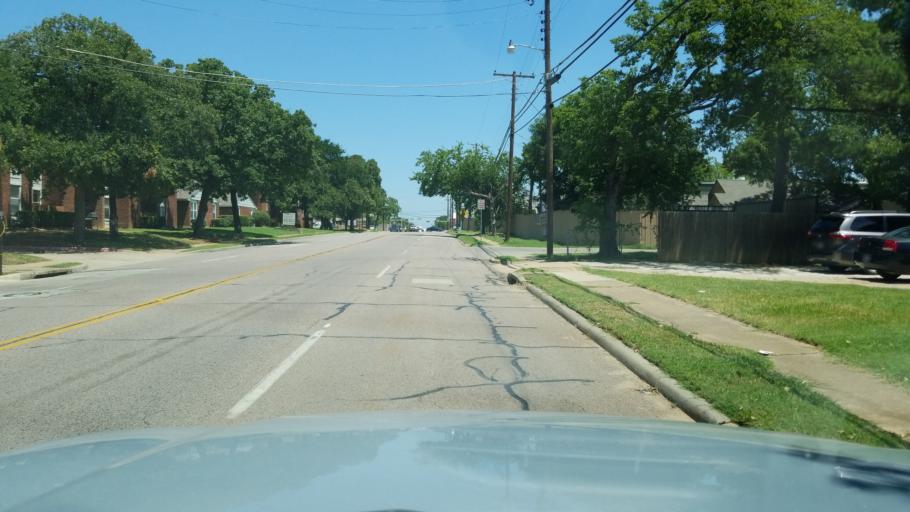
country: US
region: Texas
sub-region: Dallas County
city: Irving
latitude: 32.8061
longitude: -96.9256
